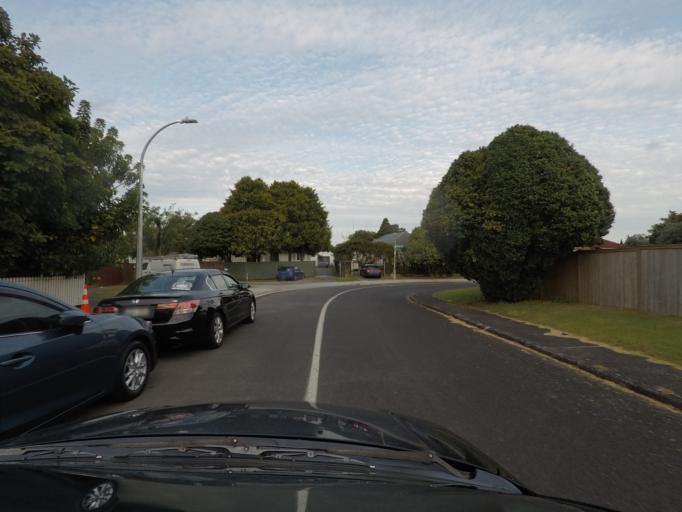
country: NZ
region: Auckland
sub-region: Auckland
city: Rosebank
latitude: -36.8349
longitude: 174.6529
